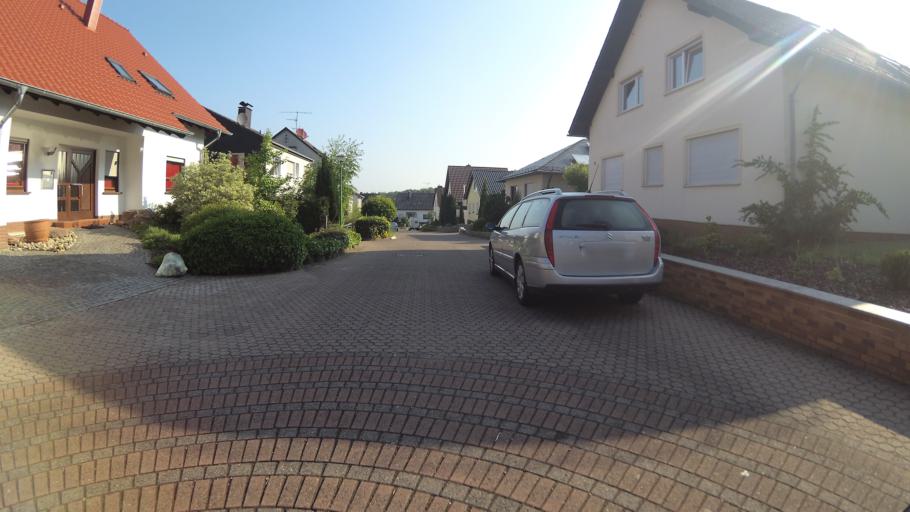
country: DE
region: Saarland
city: Kirkel
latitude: 49.2877
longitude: 7.2410
